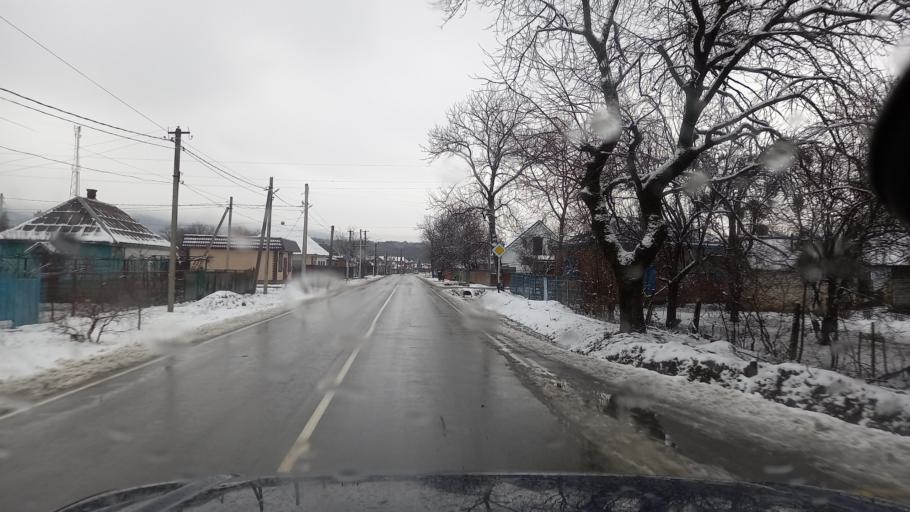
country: RU
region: Adygeya
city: Abadzekhskaya
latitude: 44.3902
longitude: 40.2218
